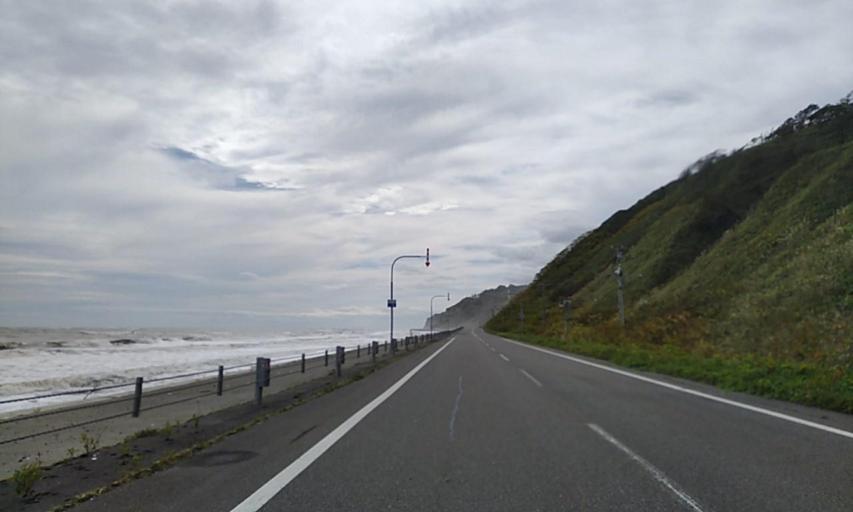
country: JP
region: Hokkaido
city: Obihiro
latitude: 42.7793
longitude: 143.7819
